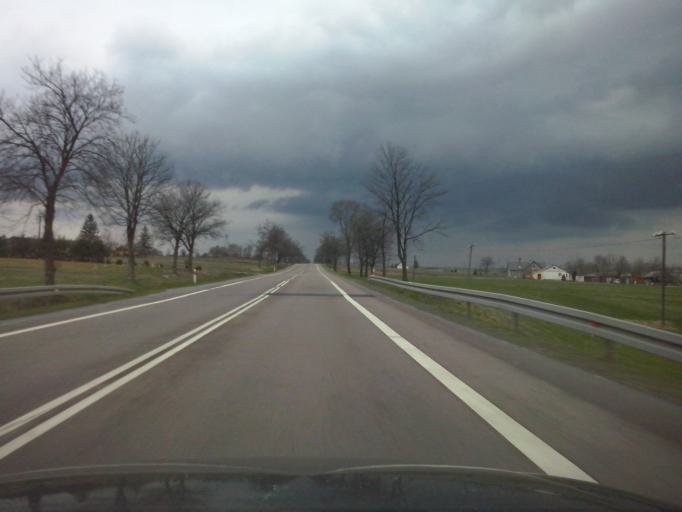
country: PL
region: Lublin Voivodeship
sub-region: Powiat chelmski
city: Rejowiec Fabryczny
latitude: 51.1759
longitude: 23.2439
